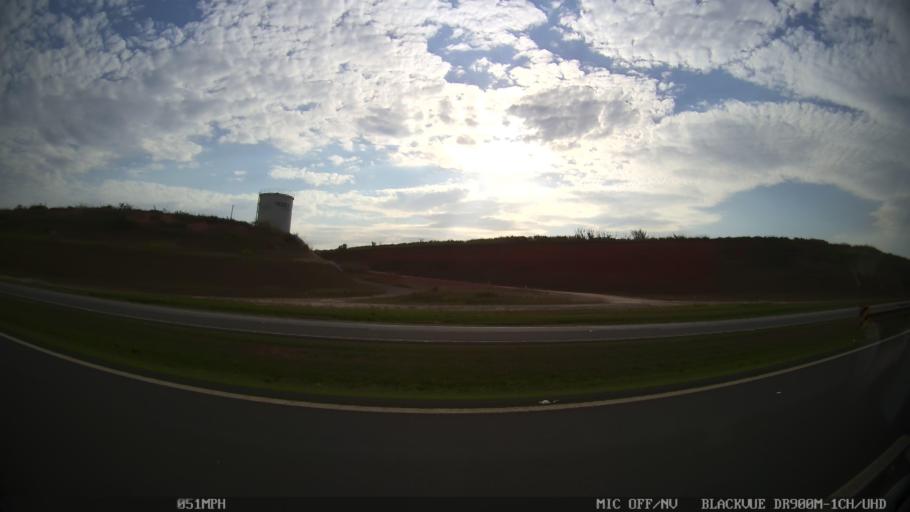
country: BR
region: Sao Paulo
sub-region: Cosmopolis
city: Cosmopolis
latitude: -22.6229
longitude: -47.2008
